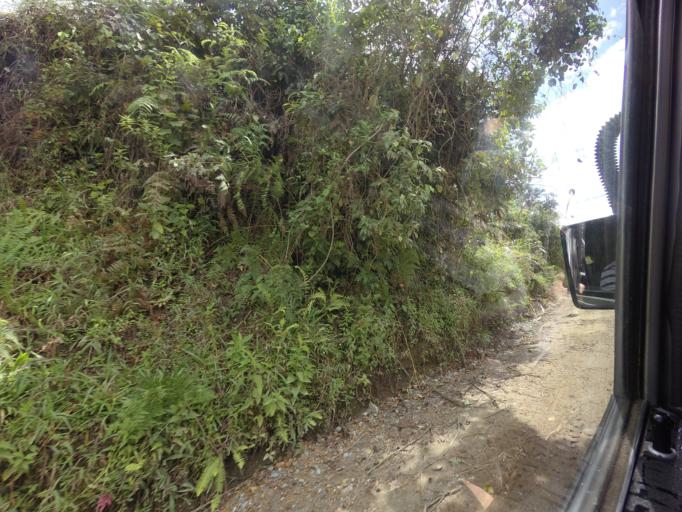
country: CO
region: Huila
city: Isnos
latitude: 1.9409
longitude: -76.2680
